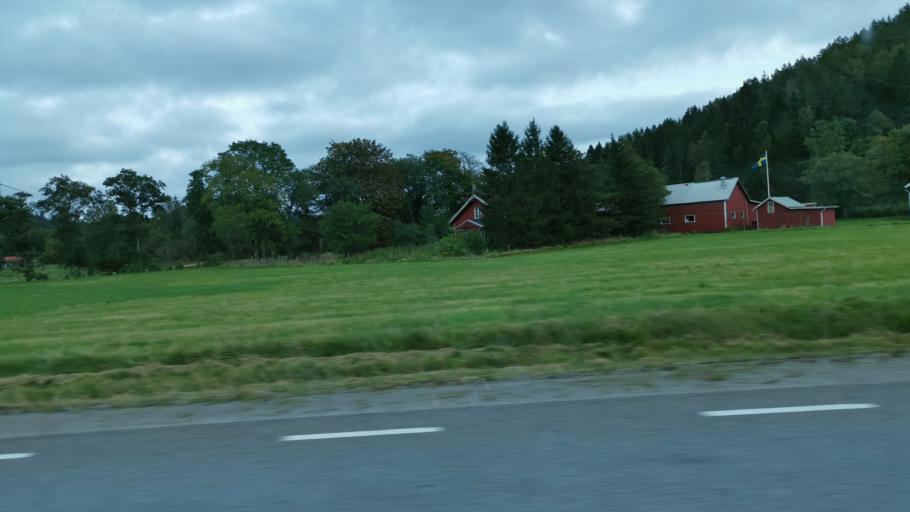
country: SE
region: Vaestra Goetaland
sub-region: Lysekils Kommun
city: Brastad
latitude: 58.5609
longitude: 11.4714
